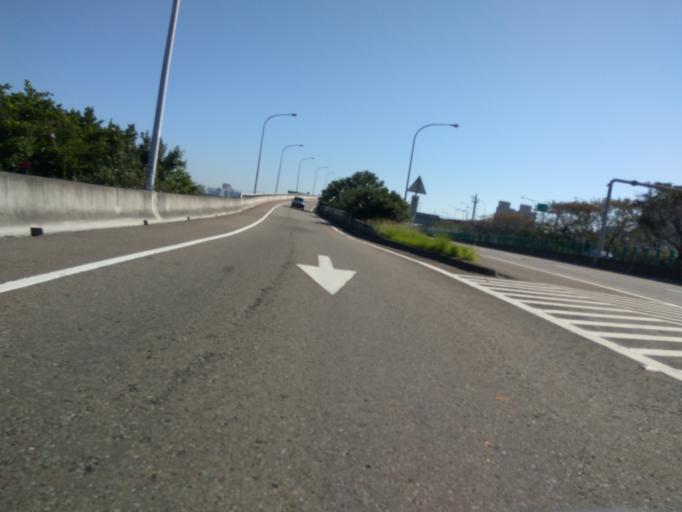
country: TW
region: Taiwan
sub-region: Hsinchu
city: Hsinchu
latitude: 24.8270
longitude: 120.9692
